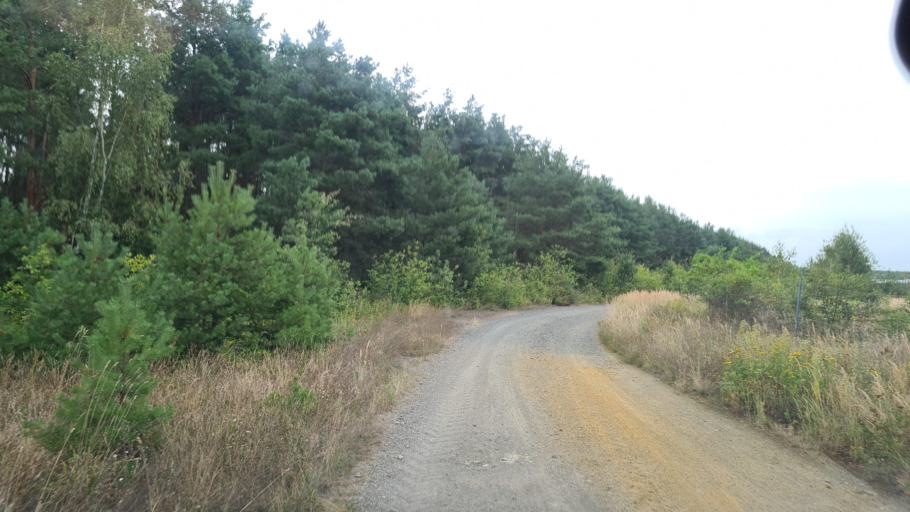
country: DE
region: Brandenburg
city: Finsterwalde
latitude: 51.5696
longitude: 13.7280
